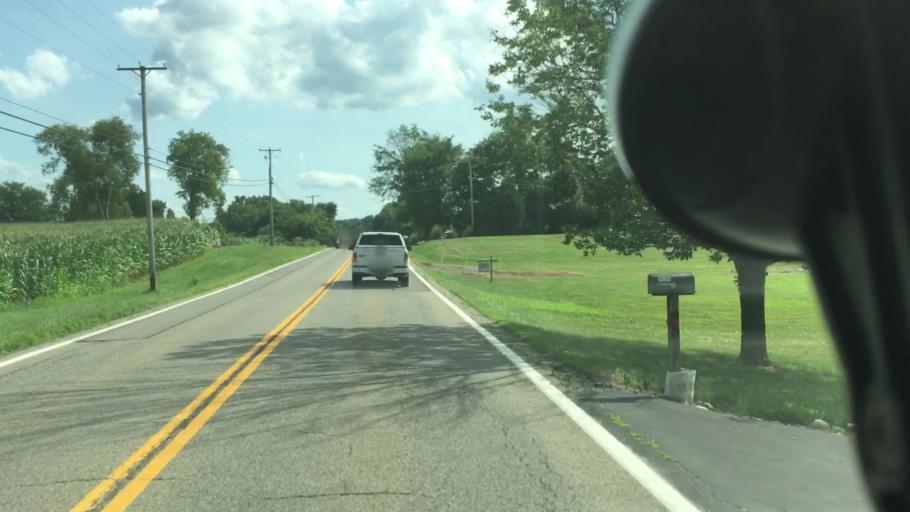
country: US
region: Ohio
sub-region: Columbiana County
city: Salem
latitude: 40.9548
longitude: -80.8324
